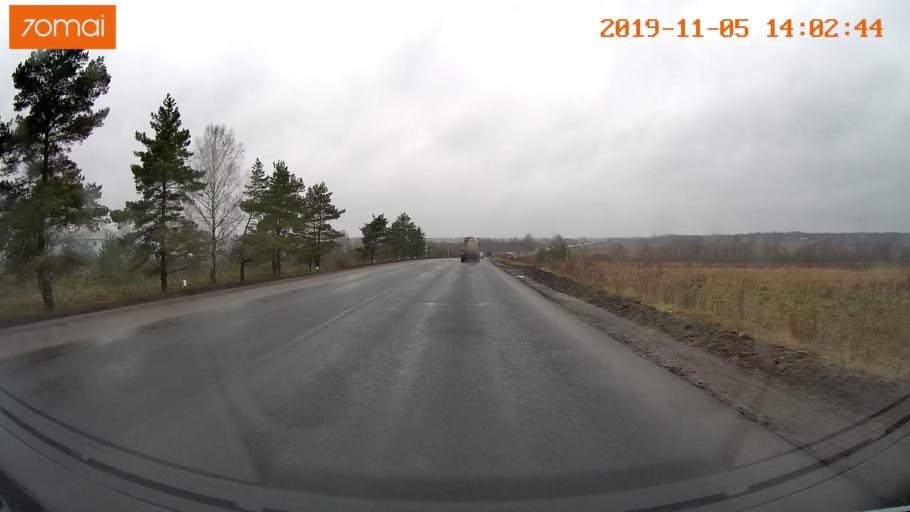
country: RU
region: Ivanovo
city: Kokhma
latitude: 57.0000
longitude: 41.2084
